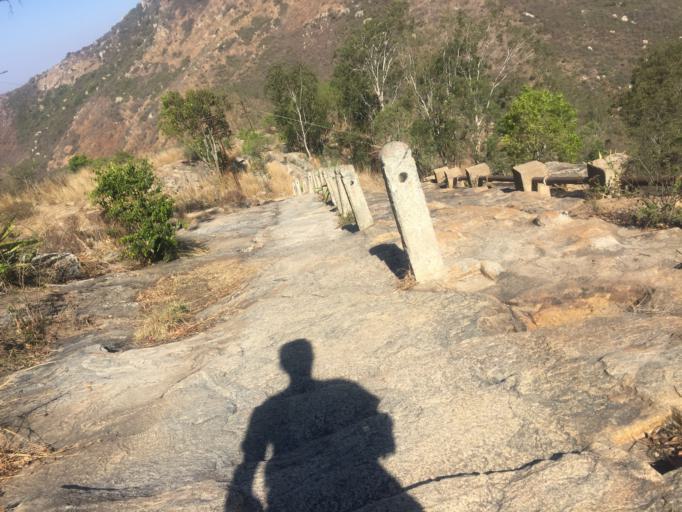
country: IN
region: Karnataka
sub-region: Chikkaballapur
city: Chik Ballapur
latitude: 13.3743
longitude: 77.6763
